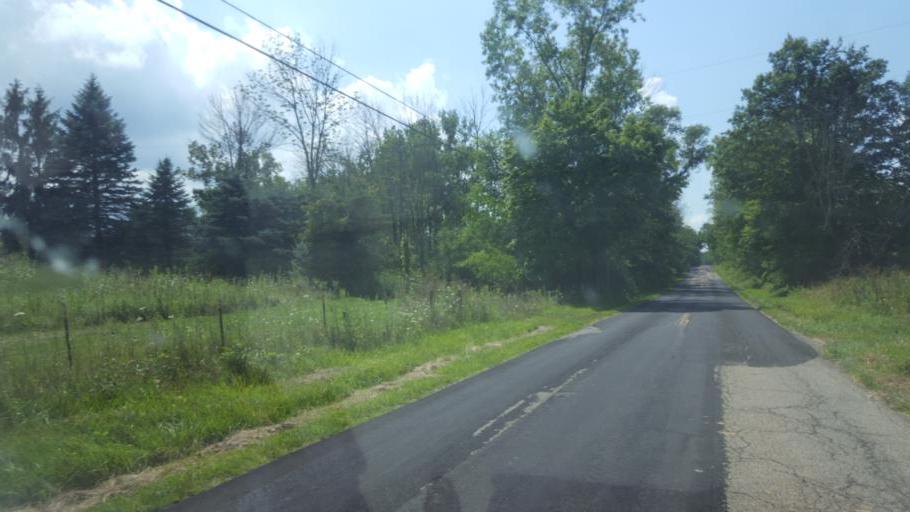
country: US
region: Ohio
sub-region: Knox County
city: Mount Vernon
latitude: 40.3776
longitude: -82.5892
